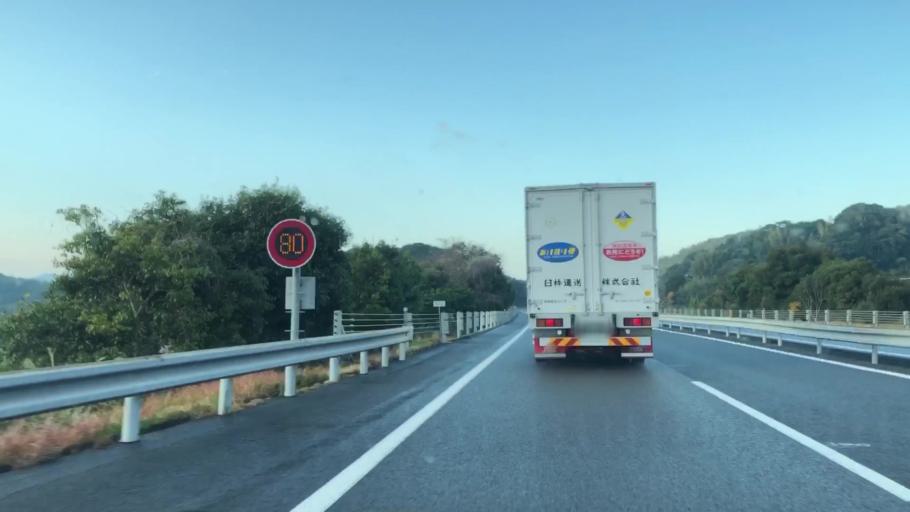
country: JP
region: Nagasaki
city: Sasebo
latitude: 33.1606
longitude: 129.8177
